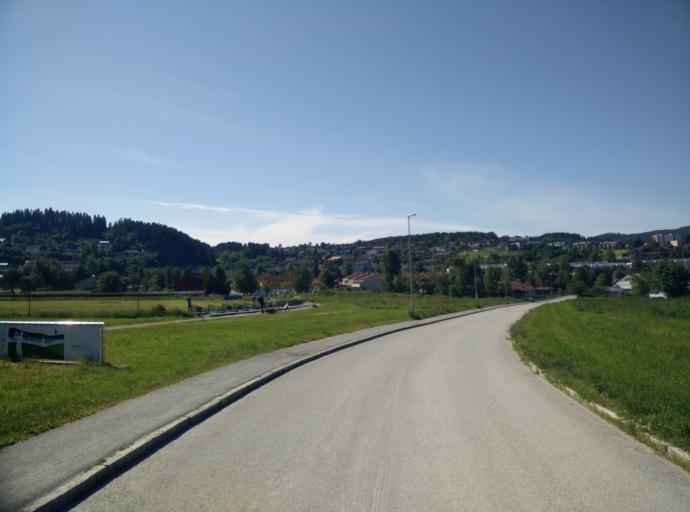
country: NO
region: Sor-Trondelag
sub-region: Trondheim
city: Trondheim
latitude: 63.4068
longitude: 10.3674
